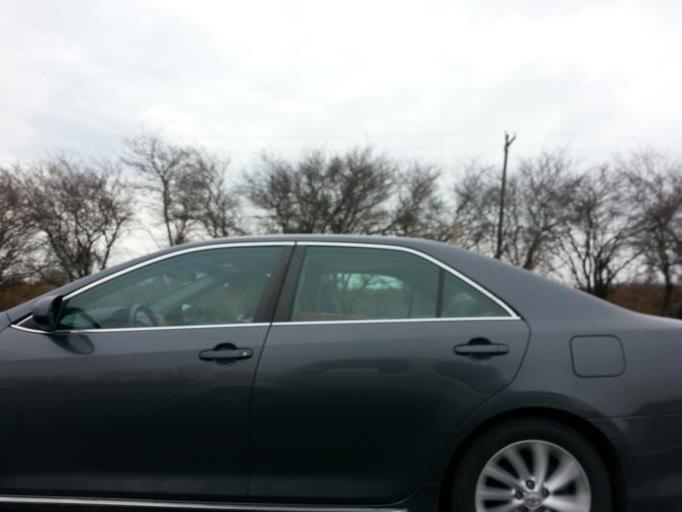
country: US
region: Indiana
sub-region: Ripley County
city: Batesville
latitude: 39.2933
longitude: -85.1780
